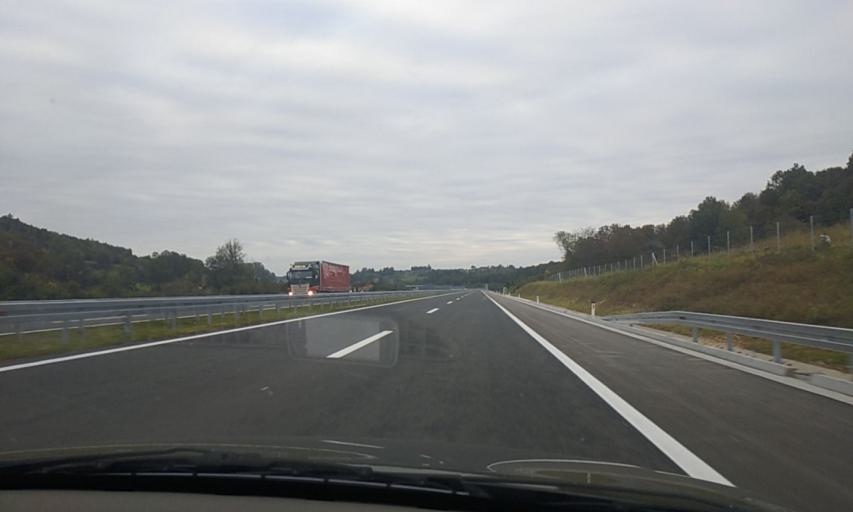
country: BA
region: Republika Srpska
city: Maglajani
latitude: 44.8609
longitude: 17.4394
